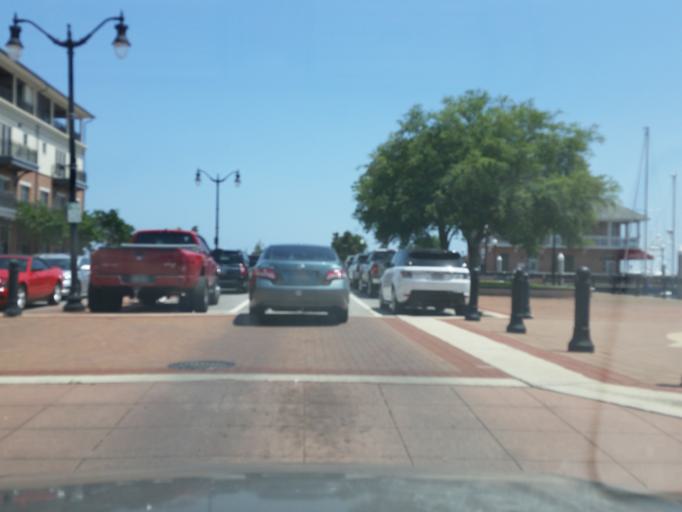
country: US
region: Florida
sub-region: Escambia County
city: Pensacola
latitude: 30.4035
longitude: -87.2133
